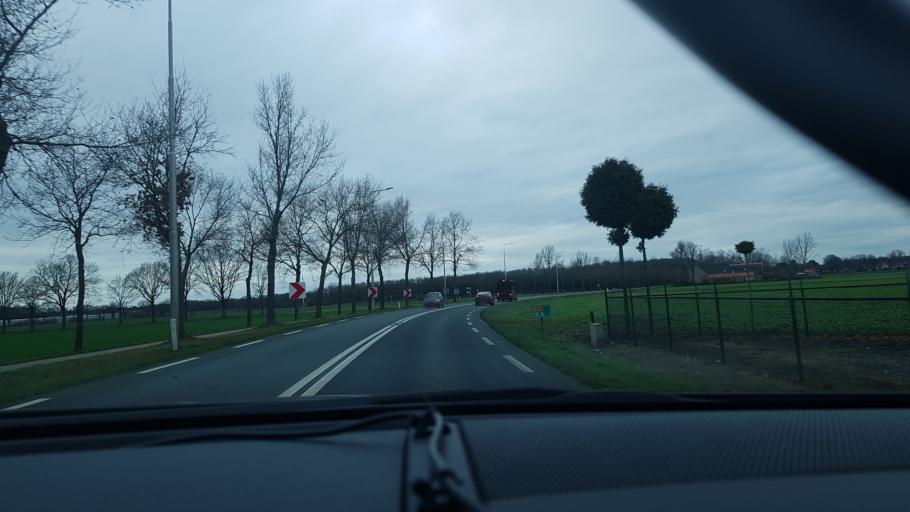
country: NL
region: Limburg
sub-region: Gemeente Leudal
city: Heythuysen
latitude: 51.2913
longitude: 5.8995
